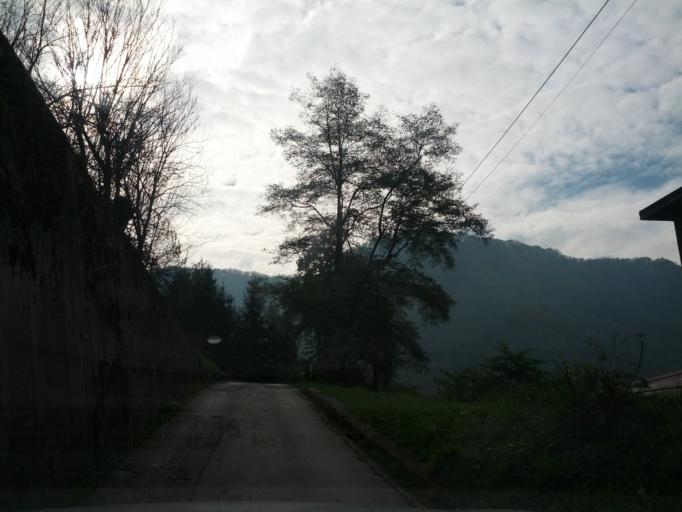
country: SI
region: Hrastnik
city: Hrastnik
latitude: 46.1242
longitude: 15.0939
